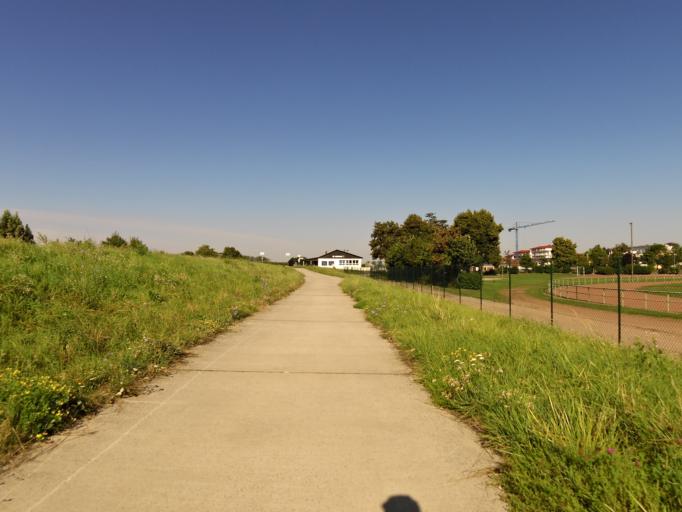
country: DE
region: Hesse
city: Biebesheim
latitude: 49.7706
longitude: 8.4718
